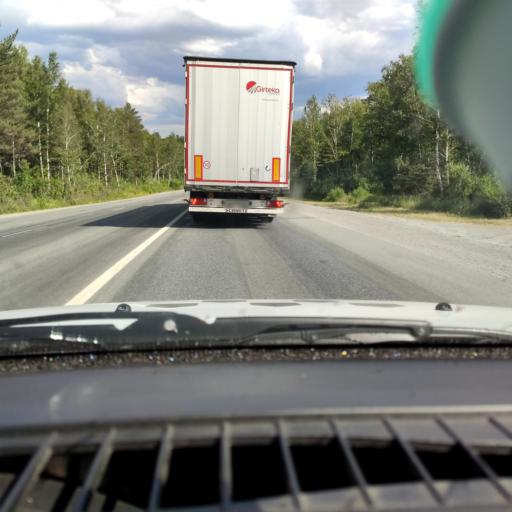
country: RU
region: Chelyabinsk
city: Syrostan
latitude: 55.0149
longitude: 59.7914
